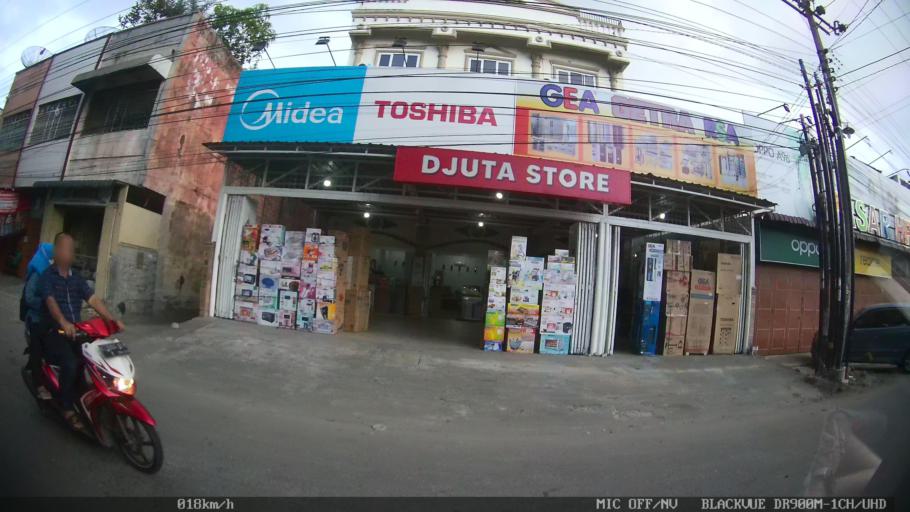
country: ID
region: North Sumatra
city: Medan
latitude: 3.5819
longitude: 98.7087
